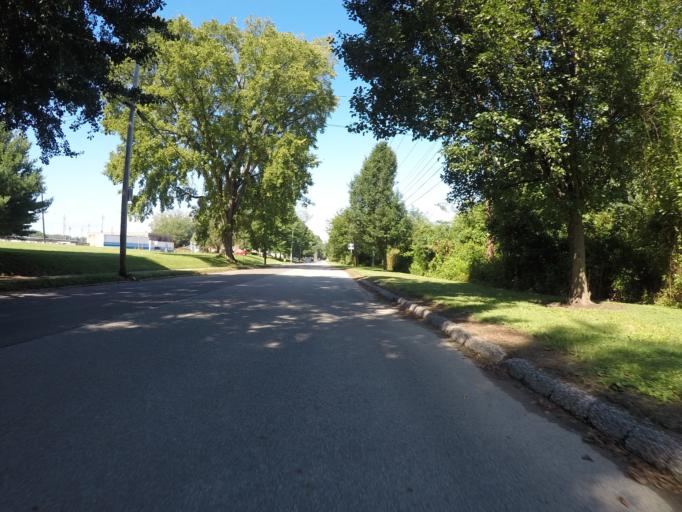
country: US
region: West Virginia
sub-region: Wayne County
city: Ceredo
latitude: 38.3995
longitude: -82.5650
